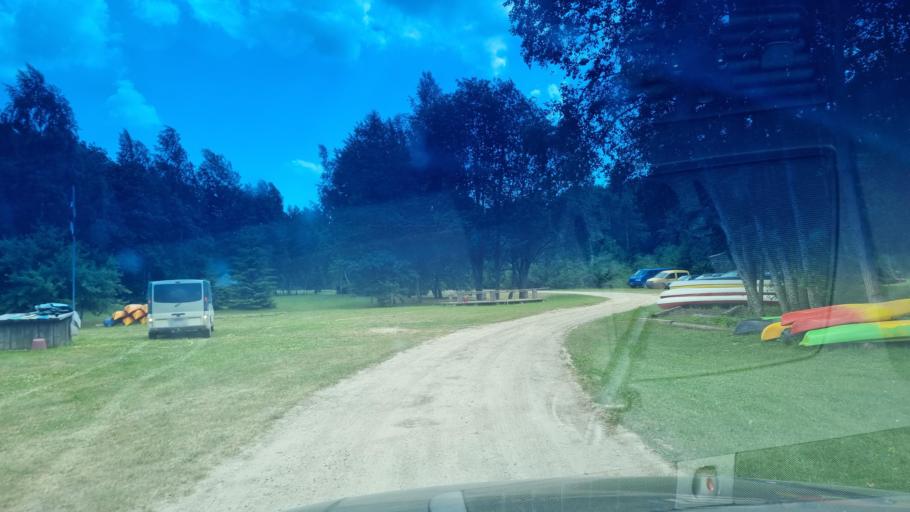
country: LV
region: Talsu Rajons
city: Stende
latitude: 57.0696
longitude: 22.2743
